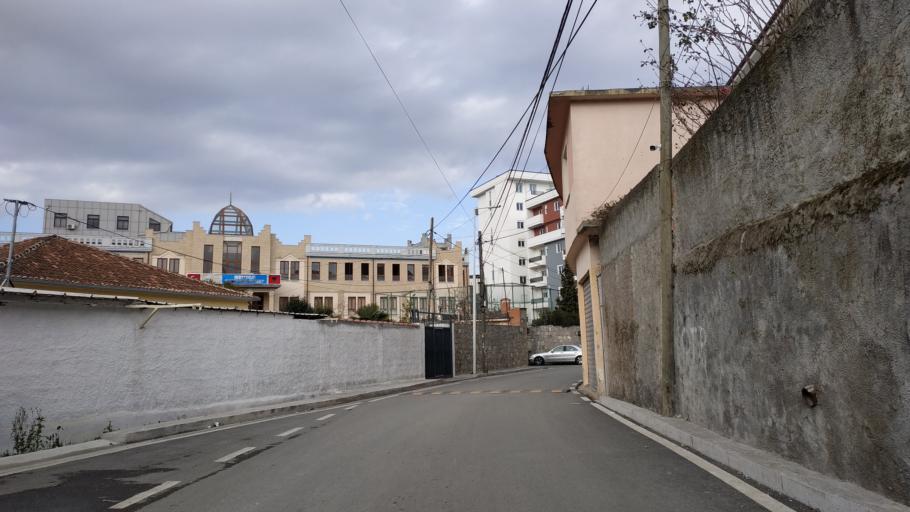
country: AL
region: Shkoder
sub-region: Rrethi i Shkodres
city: Shkoder
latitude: 42.0563
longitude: 19.5029
